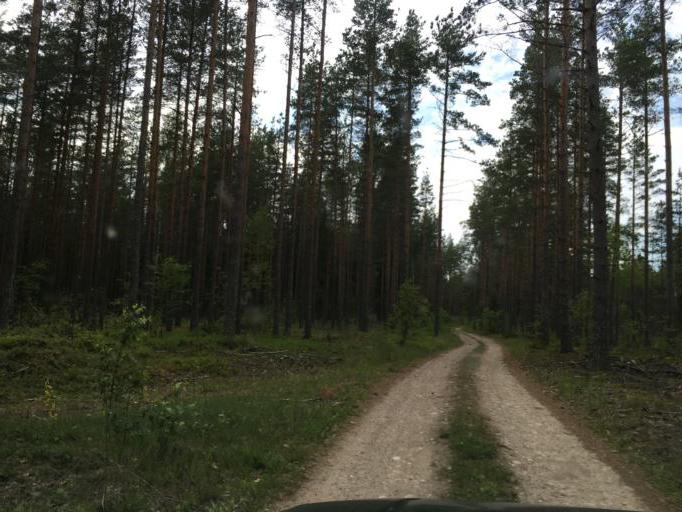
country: LV
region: Vilanu
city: Vilani
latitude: 56.7176
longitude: 26.9453
